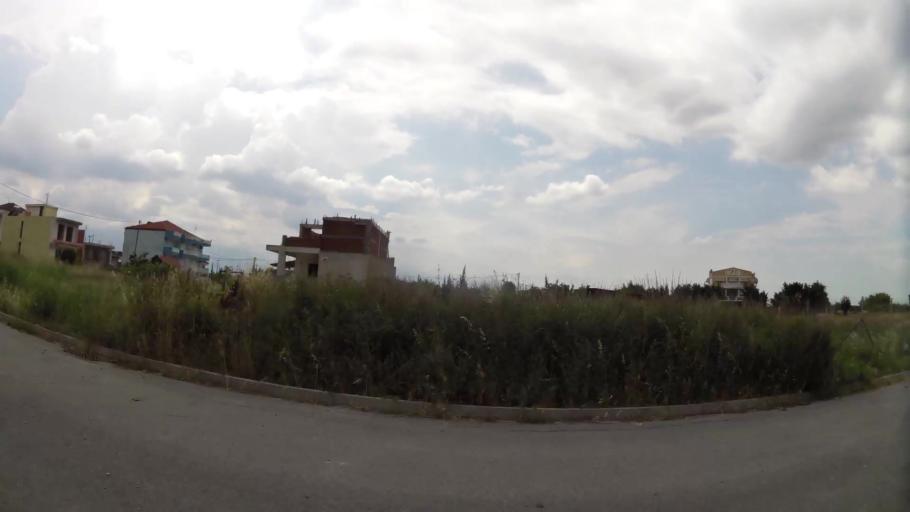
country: GR
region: Central Macedonia
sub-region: Nomos Pierias
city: Paralia
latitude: 40.2768
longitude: 22.5951
